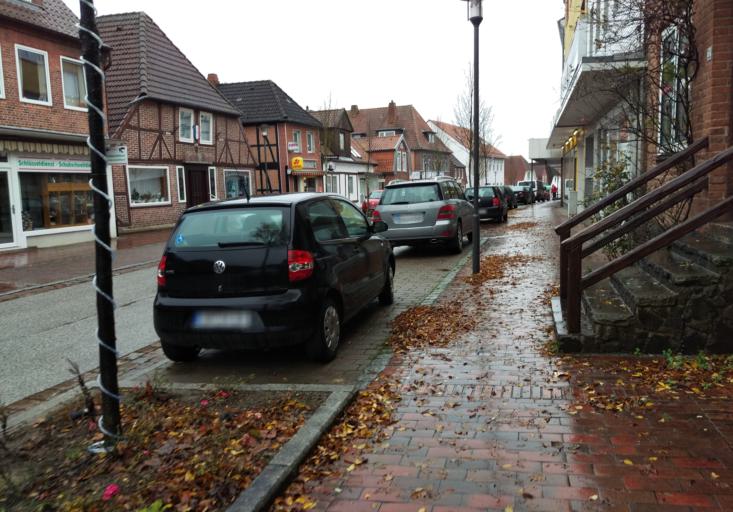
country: DE
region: Schleswig-Holstein
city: Oldenburg in Holstein
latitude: 54.2895
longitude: 10.8843
